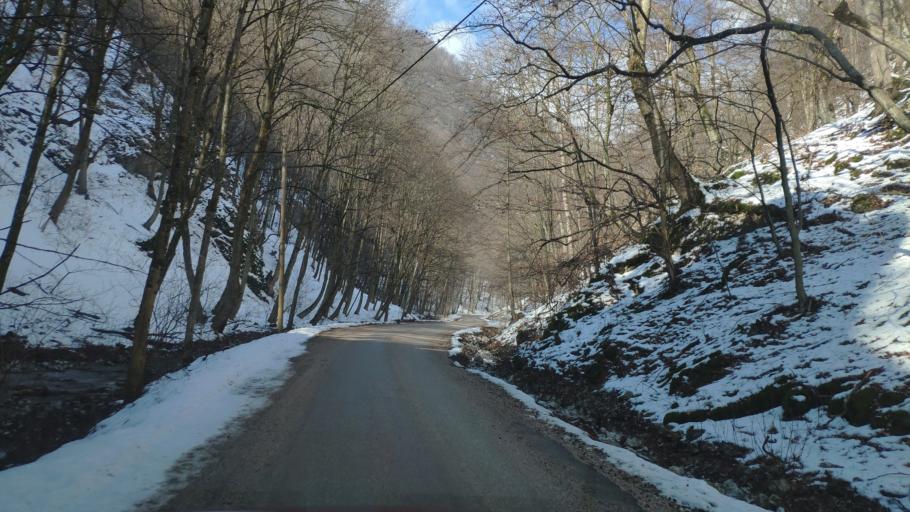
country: SK
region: Kosicky
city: Medzev
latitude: 48.6470
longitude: 20.8471
